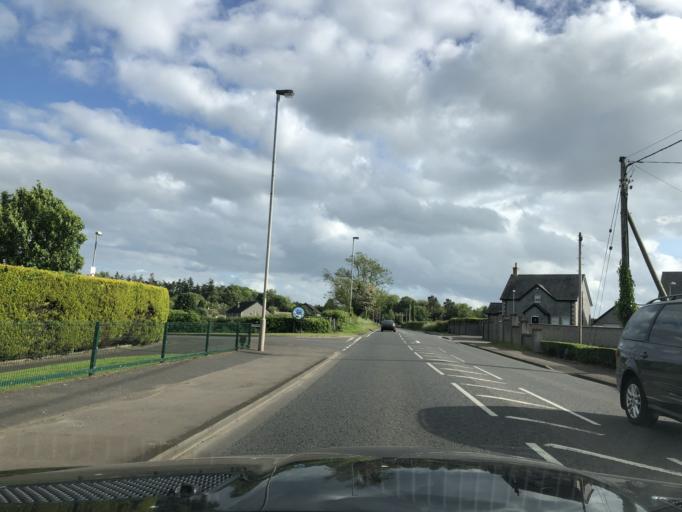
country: GB
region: Northern Ireland
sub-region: Antrim Borough
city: Antrim
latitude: 54.7057
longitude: -6.2226
